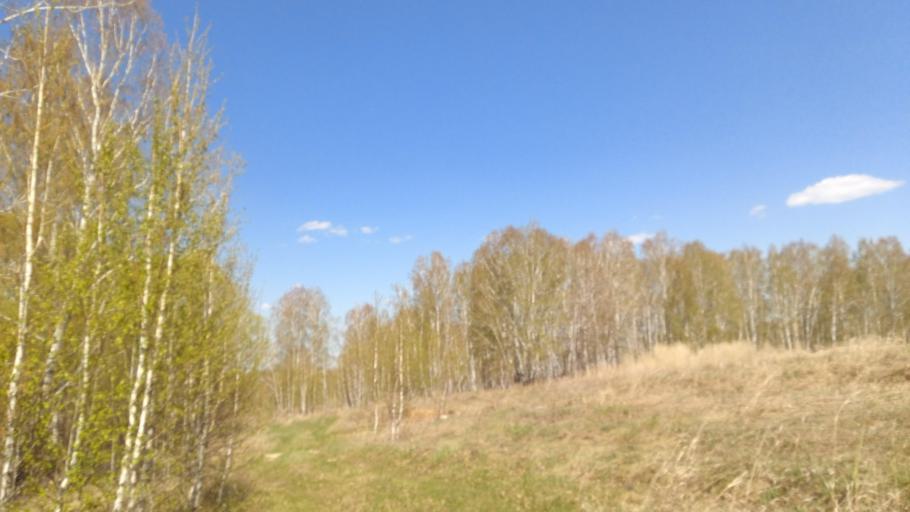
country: RU
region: Chelyabinsk
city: Timiryazevskiy
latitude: 55.0003
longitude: 60.8518
